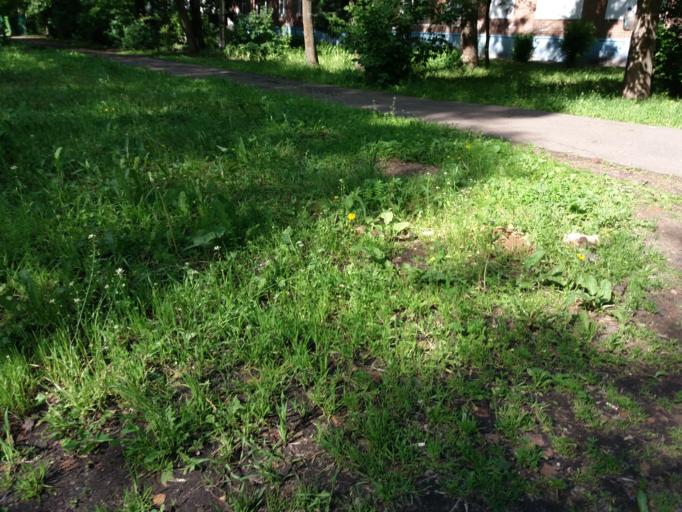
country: RU
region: Jaroslavl
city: Yaroslavl
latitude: 57.6359
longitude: 39.8529
